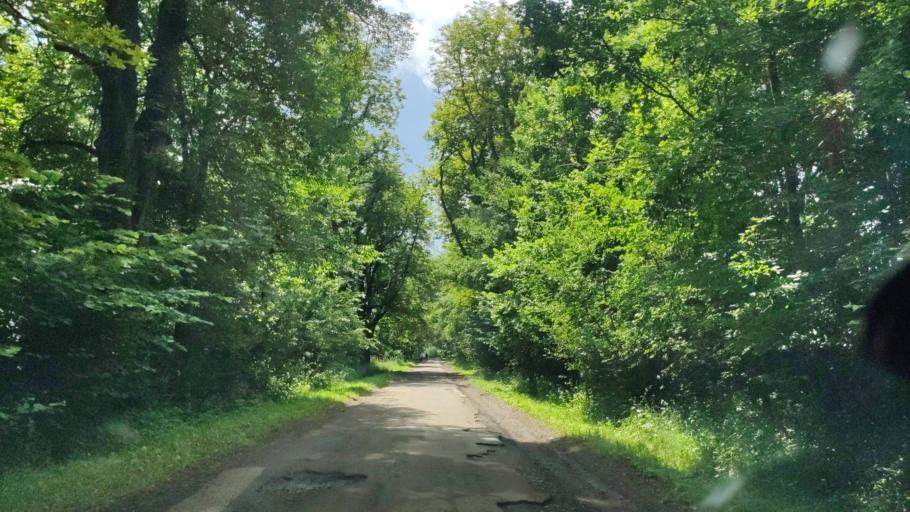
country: HU
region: Heves
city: Parad
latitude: 47.9073
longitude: 20.0559
